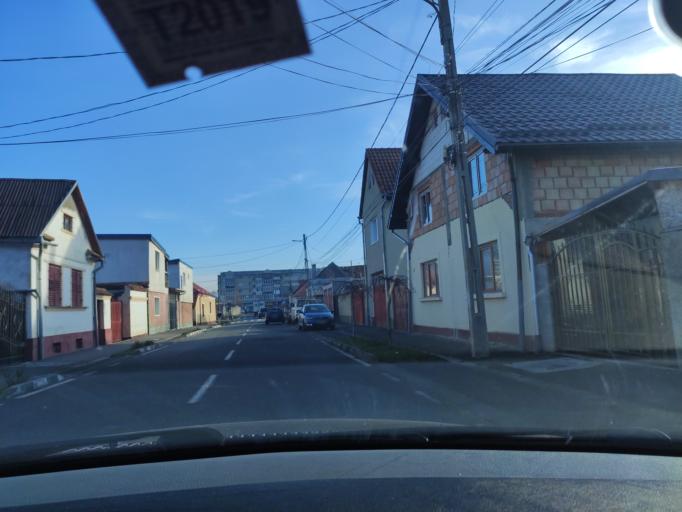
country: RO
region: Brasov
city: Codlea
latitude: 45.6928
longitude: 25.4443
